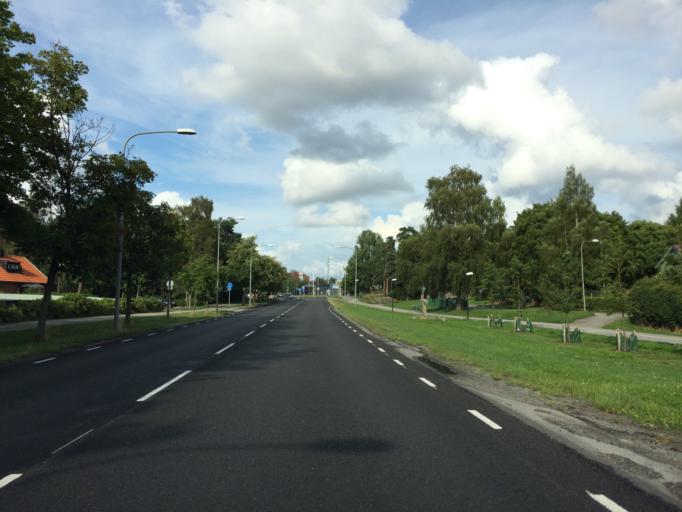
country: SE
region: Stockholm
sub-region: Huddinge Kommun
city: Segeltorp
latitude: 59.2865
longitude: 17.9789
